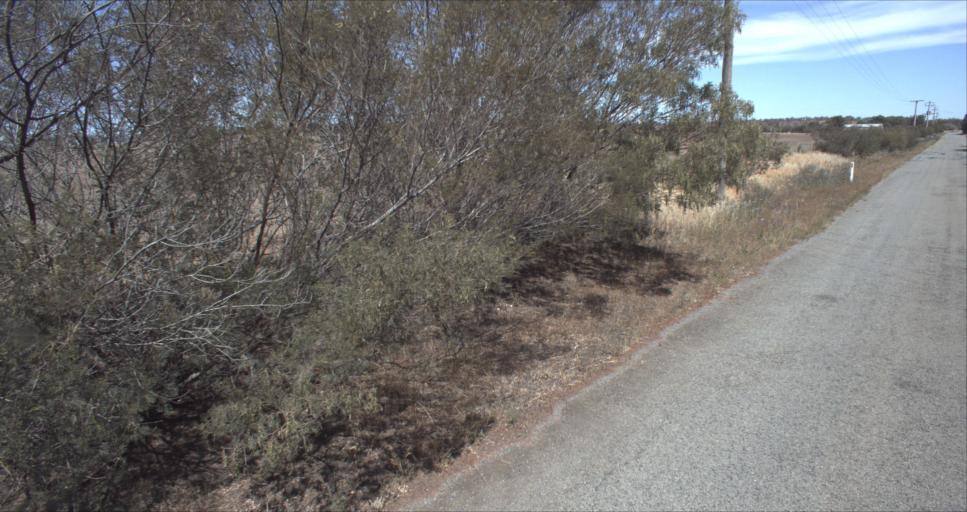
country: AU
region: New South Wales
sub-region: Leeton
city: Leeton
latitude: -34.5911
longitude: 146.4408
